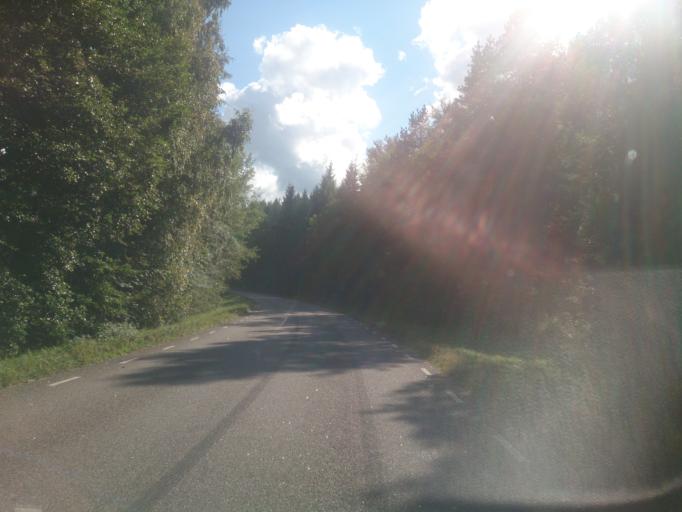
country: SE
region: OEstergoetland
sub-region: Atvidabergs Kommun
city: Atvidaberg
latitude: 58.2393
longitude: 16.0051
